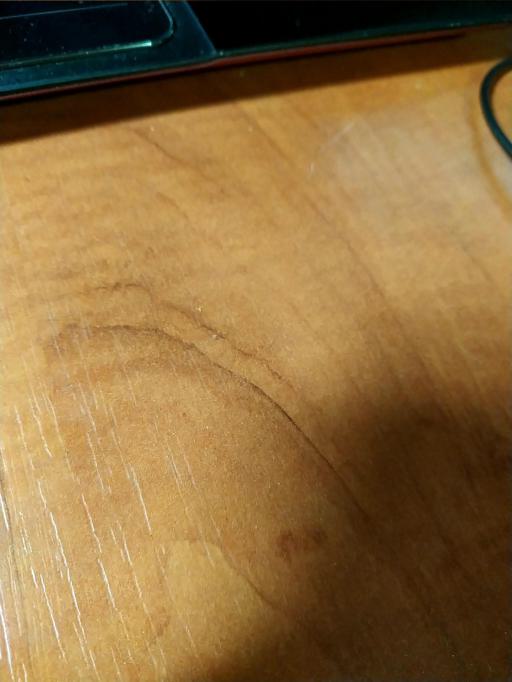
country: RU
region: Smolensk
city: Yartsevo
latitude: 55.4348
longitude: 32.7922
